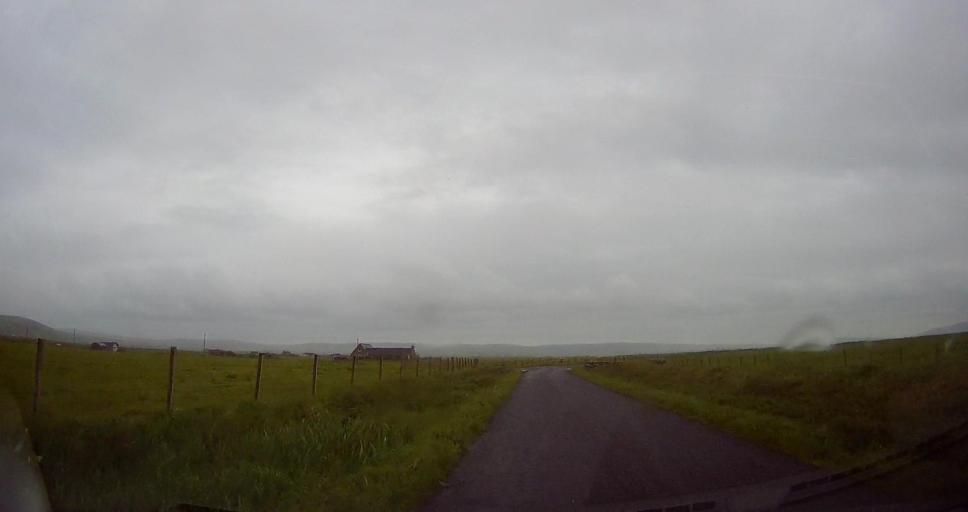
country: GB
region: Scotland
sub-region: Orkney Islands
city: Stromness
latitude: 59.0699
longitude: -3.2855
